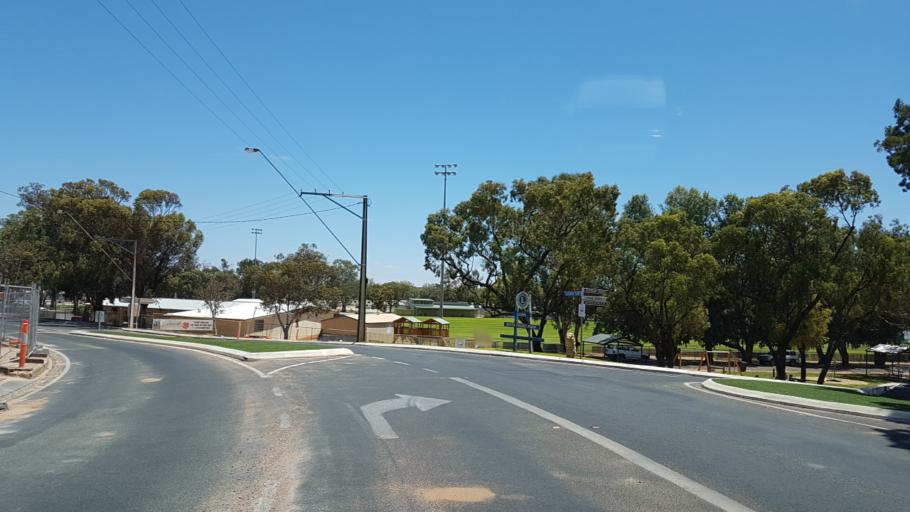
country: AU
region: South Australia
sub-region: Loxton Waikerie
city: Waikerie
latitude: -34.1766
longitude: 139.9843
